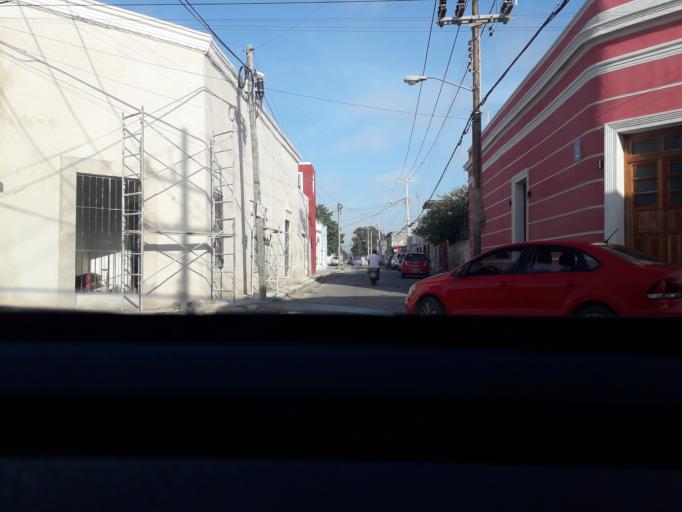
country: MX
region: Yucatan
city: Merida
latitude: 20.9605
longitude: -89.6311
